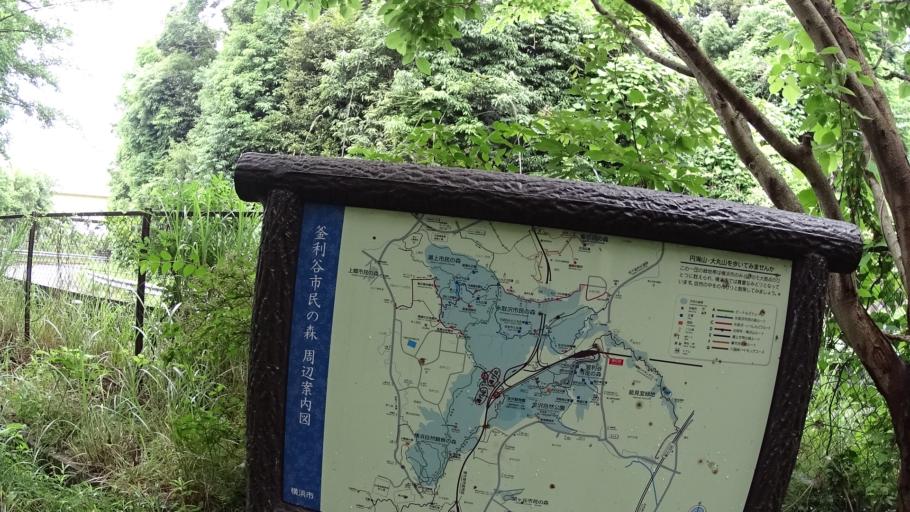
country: JP
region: Kanagawa
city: Zushi
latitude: 35.3566
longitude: 139.6053
